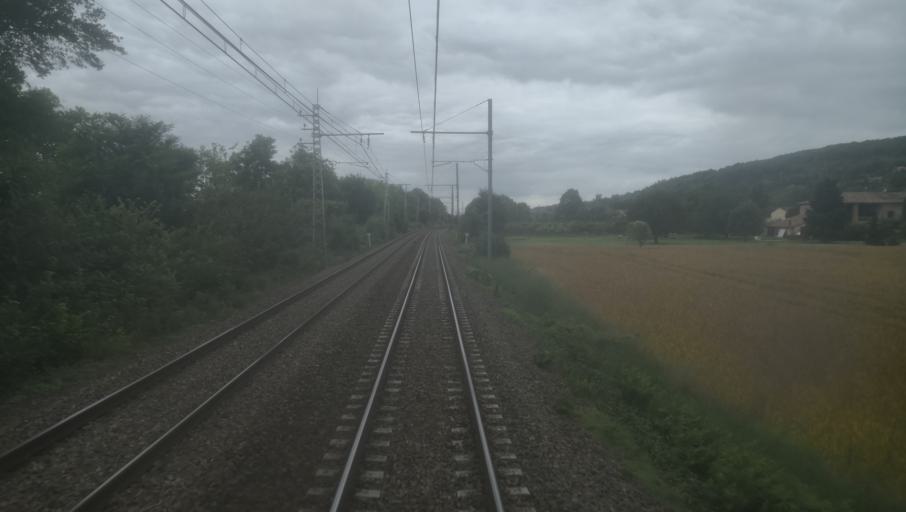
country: FR
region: Midi-Pyrenees
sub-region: Departement du Tarn-et-Garonne
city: Pompignan
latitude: 43.8000
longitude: 1.3283
